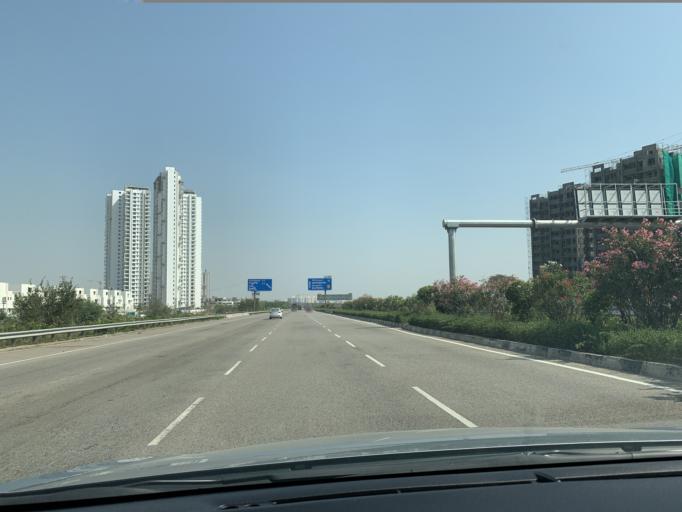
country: IN
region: Telangana
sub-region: Medak
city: Serilingampalle
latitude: 17.4015
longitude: 78.3418
